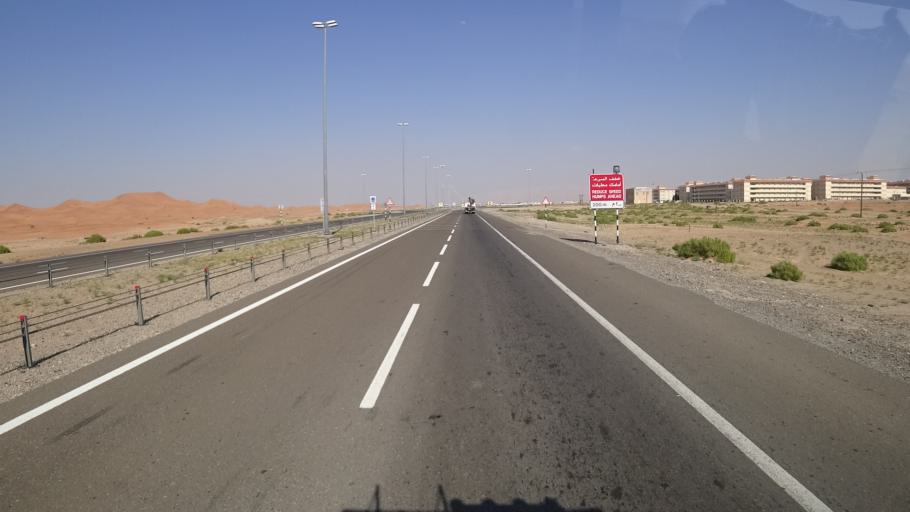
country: AE
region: Abu Dhabi
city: Al Ain
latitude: 24.0288
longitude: 55.5391
